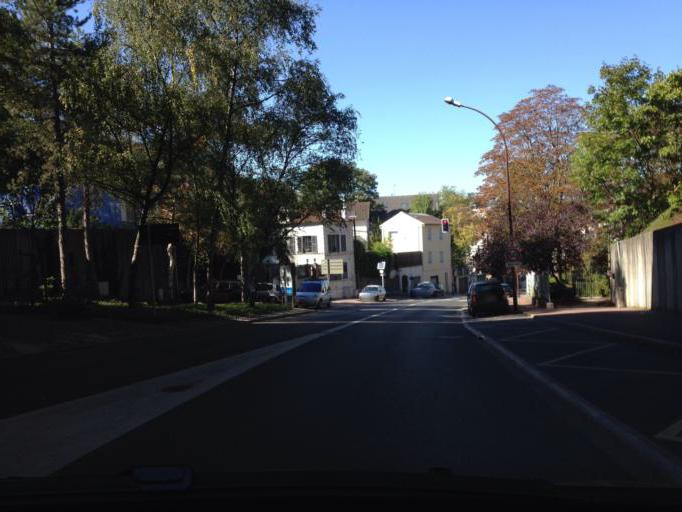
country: FR
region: Ile-de-France
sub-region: Departement des Hauts-de-Seine
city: Sevres
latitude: 48.8229
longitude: 2.2226
